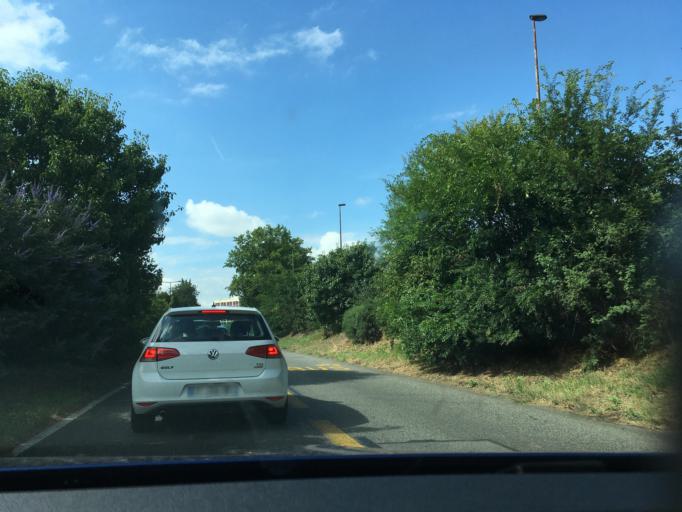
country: FR
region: Midi-Pyrenees
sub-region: Departement de la Haute-Garonne
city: Portet-sur-Garonne
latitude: 43.5758
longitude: 1.3956
